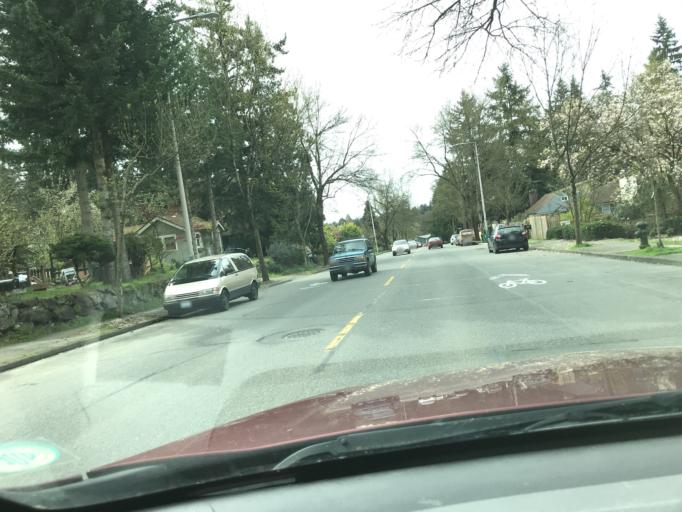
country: US
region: Washington
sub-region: King County
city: Lake Forest Park
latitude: 47.7170
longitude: -122.2913
